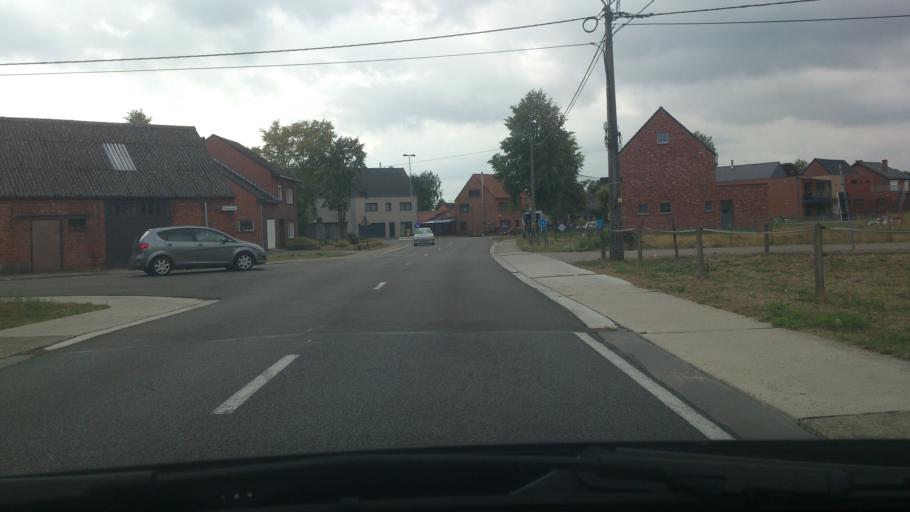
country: BE
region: Flanders
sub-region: Provincie Antwerpen
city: Mol
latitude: 51.1895
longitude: 5.0894
